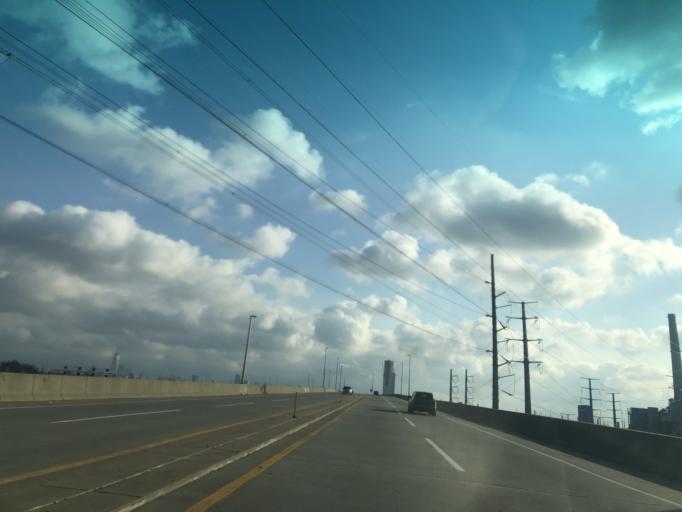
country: US
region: New Jersey
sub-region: Hudson County
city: Jersey City
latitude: 40.7537
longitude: -74.0720
